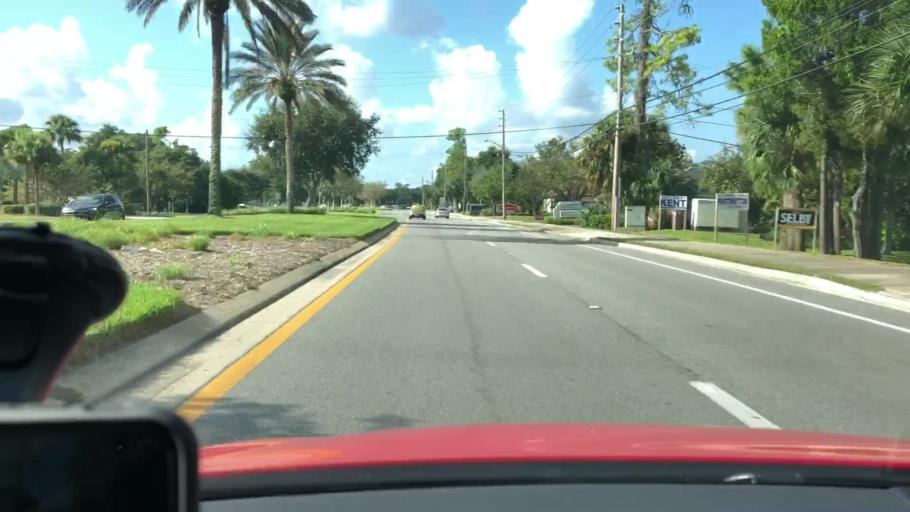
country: US
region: Florida
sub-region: Volusia County
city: Ormond Beach
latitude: 29.2621
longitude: -81.1082
